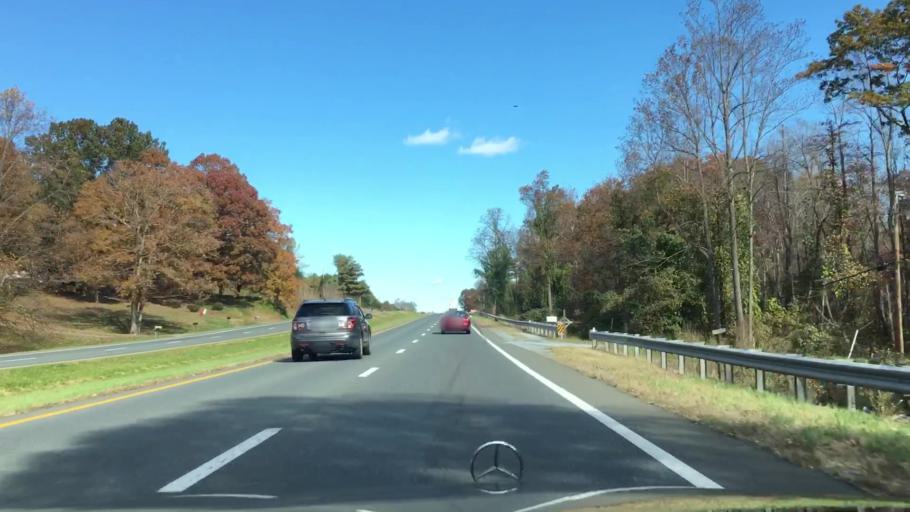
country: US
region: Virginia
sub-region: Campbell County
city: Rustburg
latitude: 37.2626
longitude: -79.1801
